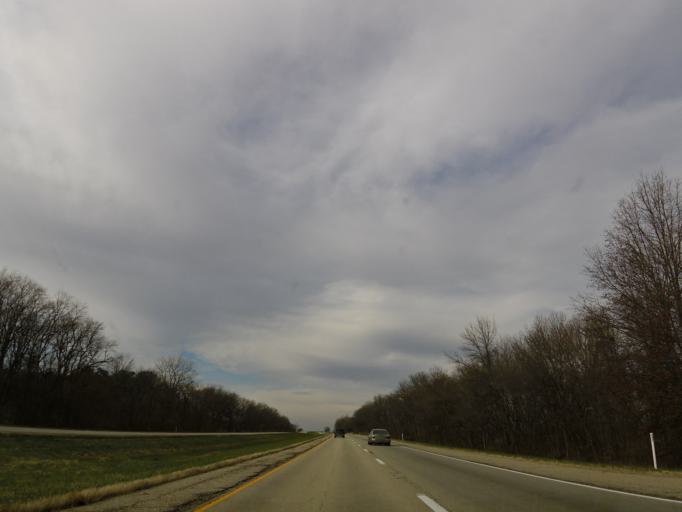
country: US
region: Illinois
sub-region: Peoria County
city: Elmwood
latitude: 40.8661
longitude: -90.0263
